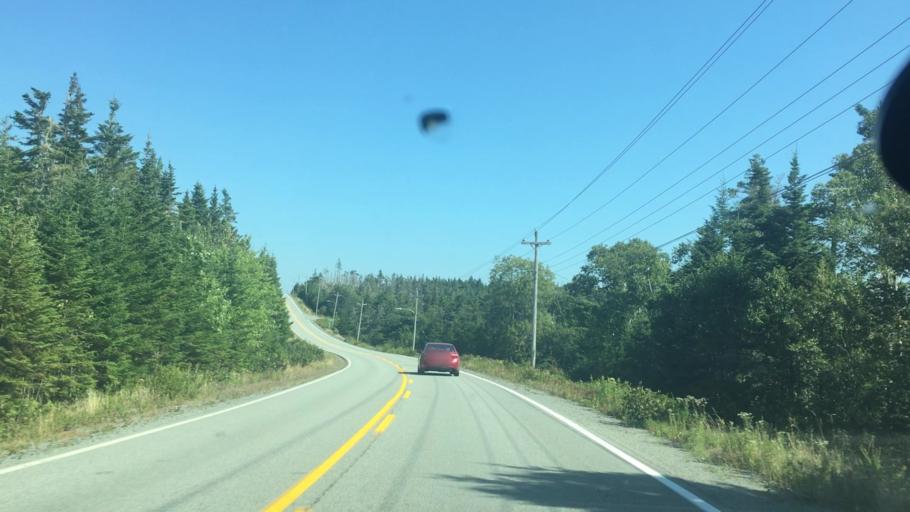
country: CA
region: Nova Scotia
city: Antigonish
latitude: 44.9355
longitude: -62.2712
